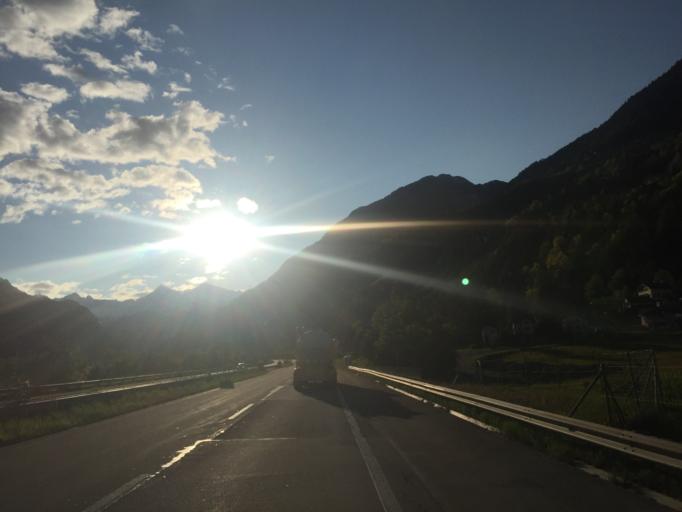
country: CH
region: Ticino
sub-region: Leventina District
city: Faido
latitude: 46.5105
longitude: 8.7072
